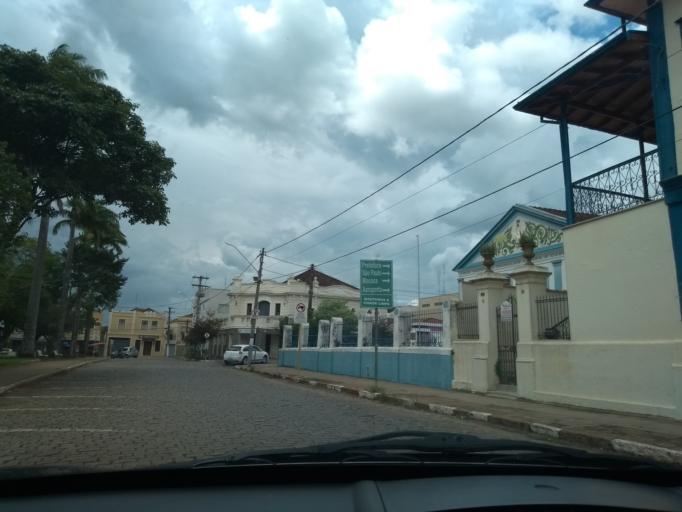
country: BR
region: Sao Paulo
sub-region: Casa Branca
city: Casa Branca
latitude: -21.7739
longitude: -47.0859
